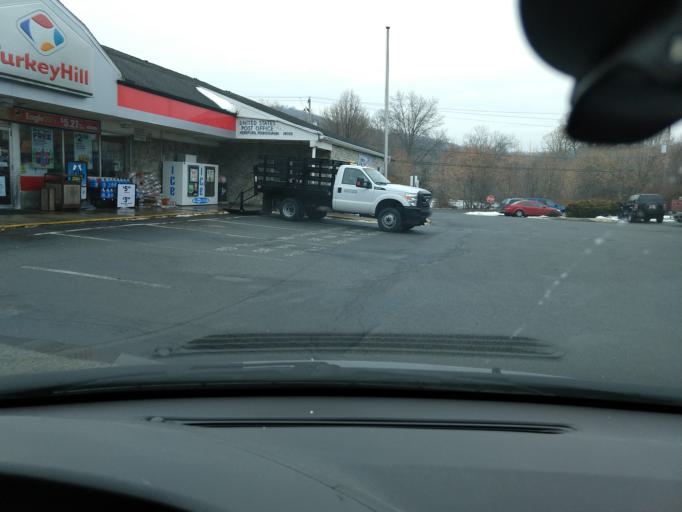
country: US
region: Pennsylvania
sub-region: Berks County
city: Bally
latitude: 40.4481
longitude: -75.5529
